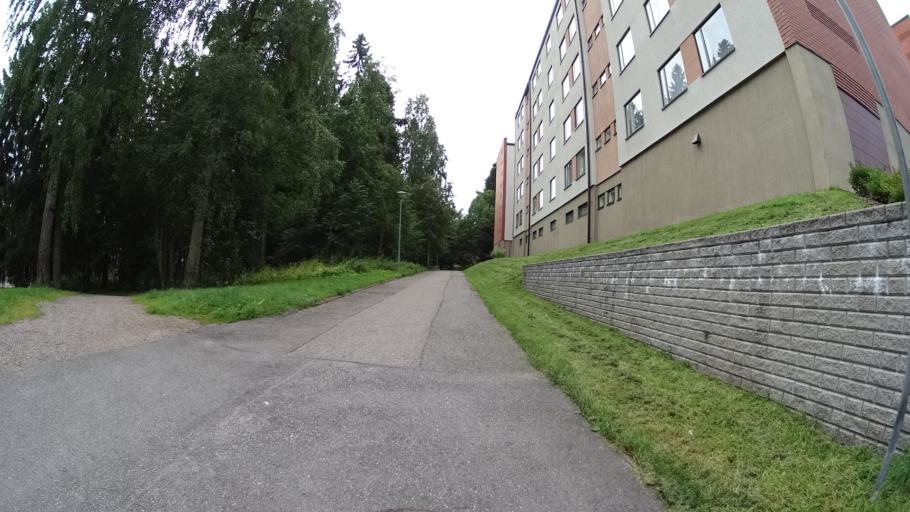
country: FI
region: Uusimaa
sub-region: Helsinki
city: Teekkarikylae
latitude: 60.2677
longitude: 24.8580
